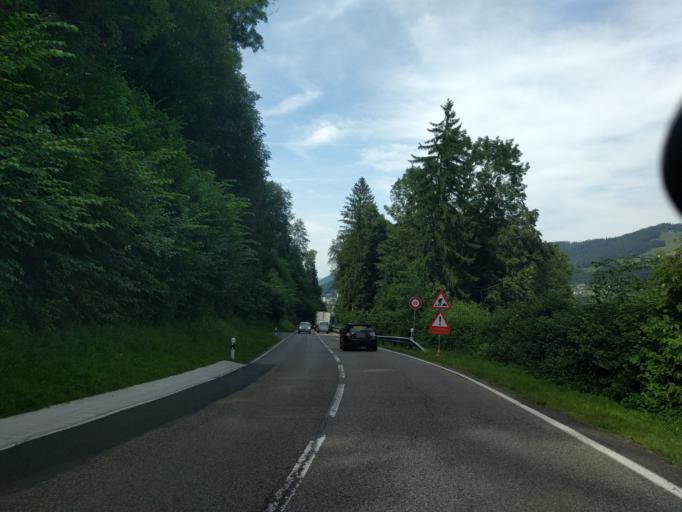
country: CH
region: Saint Gallen
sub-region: Wahlkreis Toggenburg
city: Wattwil
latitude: 47.2900
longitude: 9.0850
